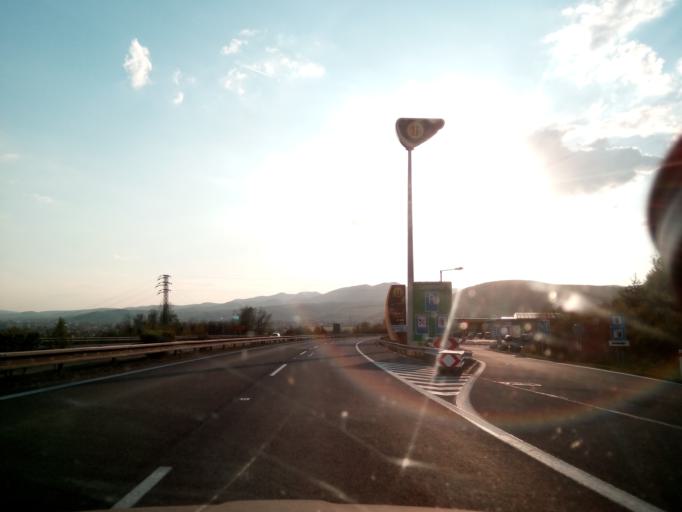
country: SK
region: Trenciansky
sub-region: Okres Trencin
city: Trencin
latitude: 48.9136
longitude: 18.0573
